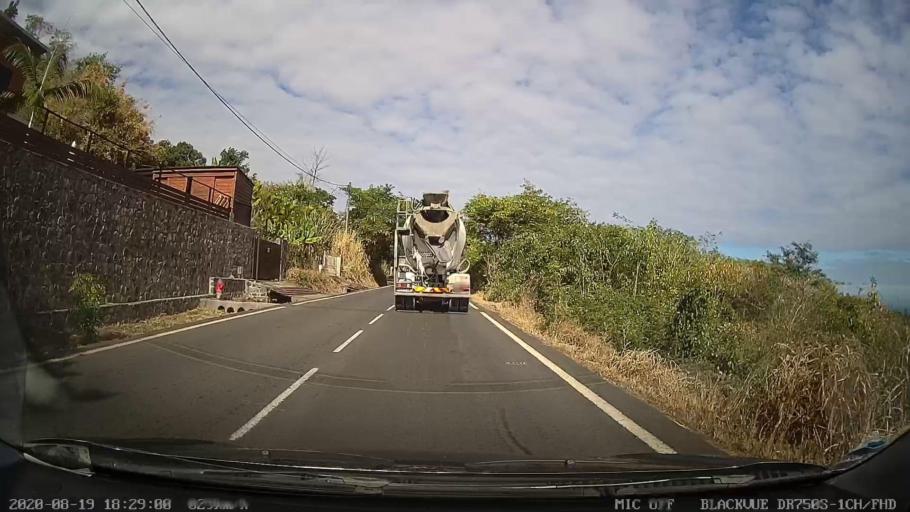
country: RE
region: Reunion
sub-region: Reunion
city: La Possession
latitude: -20.9570
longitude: 55.3503
